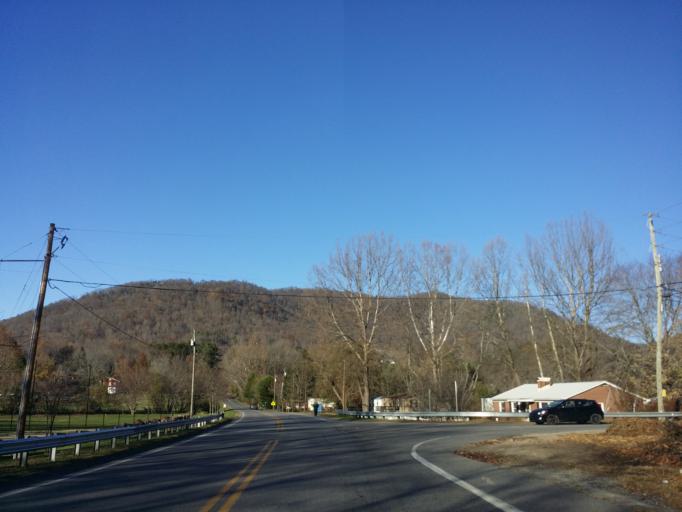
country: US
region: North Carolina
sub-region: Buncombe County
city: Swannanoa
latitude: 35.6014
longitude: -82.4082
